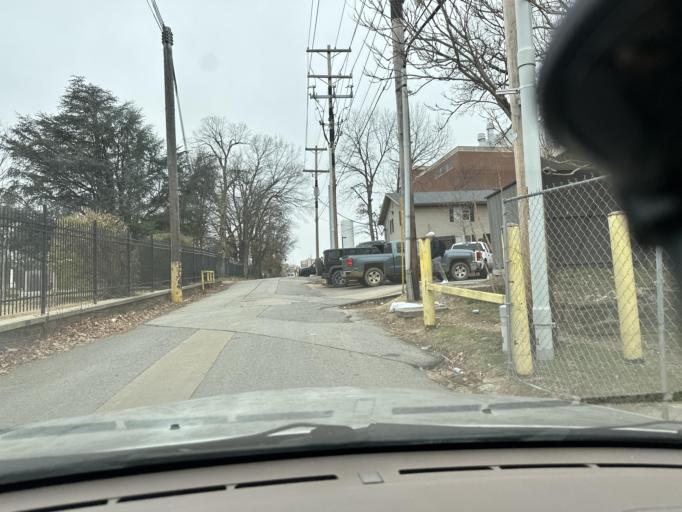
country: US
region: Arkansas
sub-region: Washington County
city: Fayetteville
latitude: 36.0655
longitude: -94.1685
